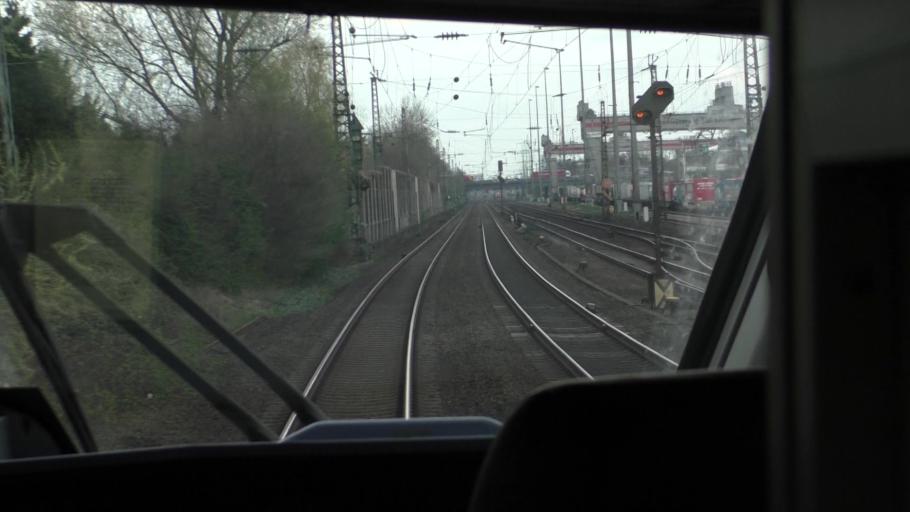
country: DE
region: North Rhine-Westphalia
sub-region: Regierungsbezirk Koln
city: Hurth
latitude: 50.8846
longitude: 6.9143
